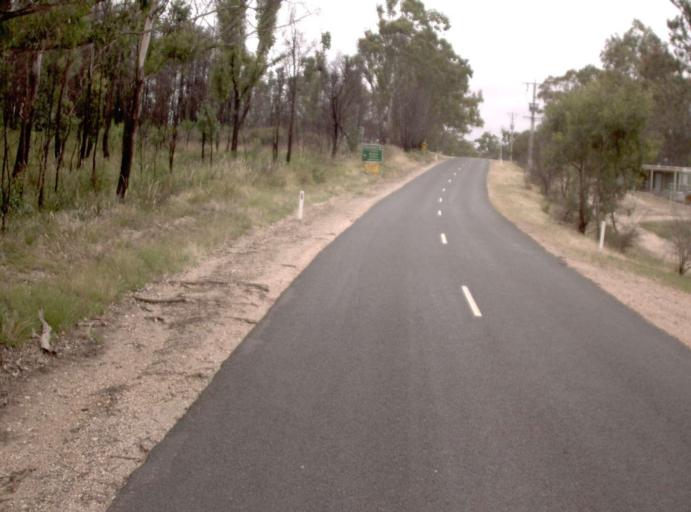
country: AU
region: Victoria
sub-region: Wellington
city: Heyfield
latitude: -37.9071
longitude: 146.7554
